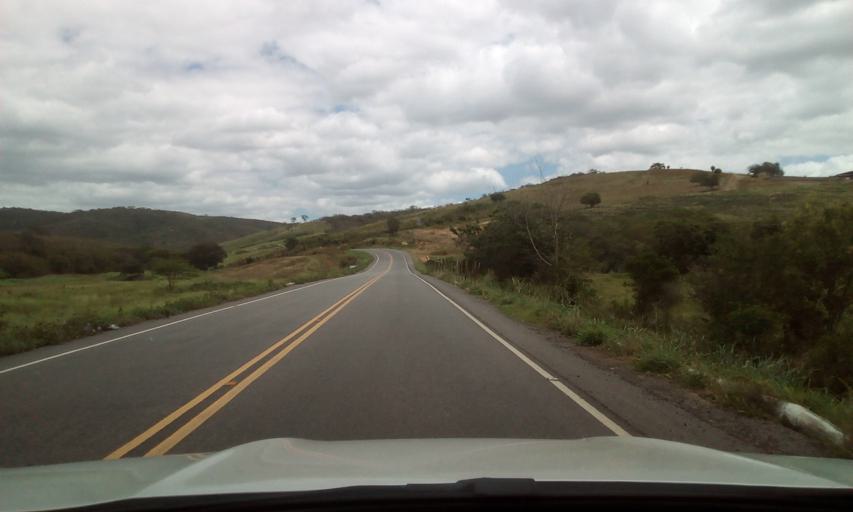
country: BR
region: Paraiba
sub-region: Serra Redonda
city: Alagoa Grande
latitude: -7.1587
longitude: -35.6015
